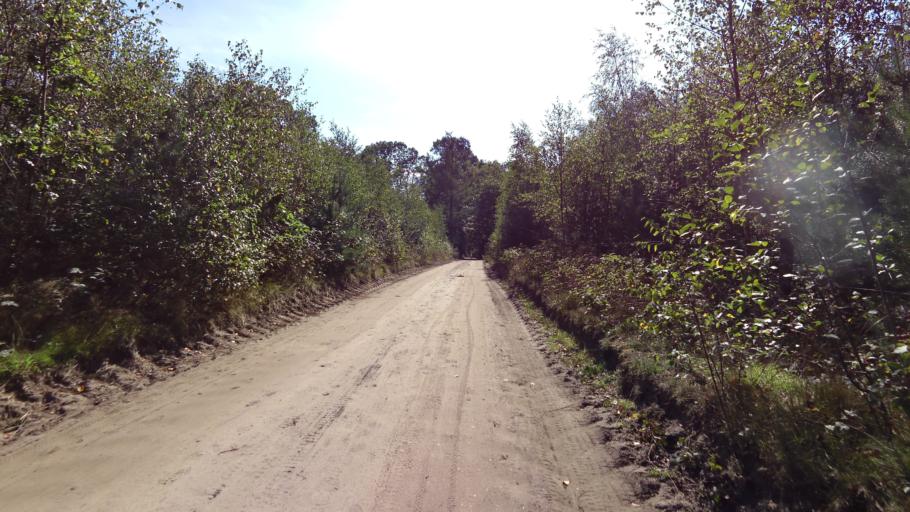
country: NL
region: Gelderland
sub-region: Gemeente Renkum
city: Renkum
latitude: 52.0020
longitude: 5.7382
